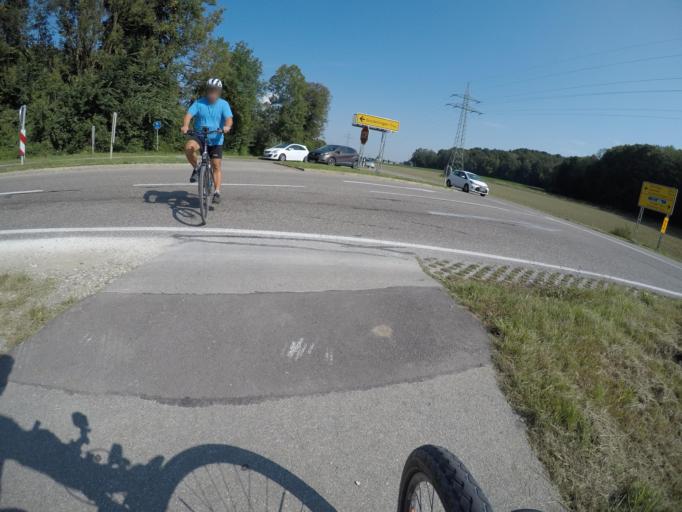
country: DE
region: Bavaria
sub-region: Swabia
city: Gundremmingen
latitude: 48.4889
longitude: 10.3869
